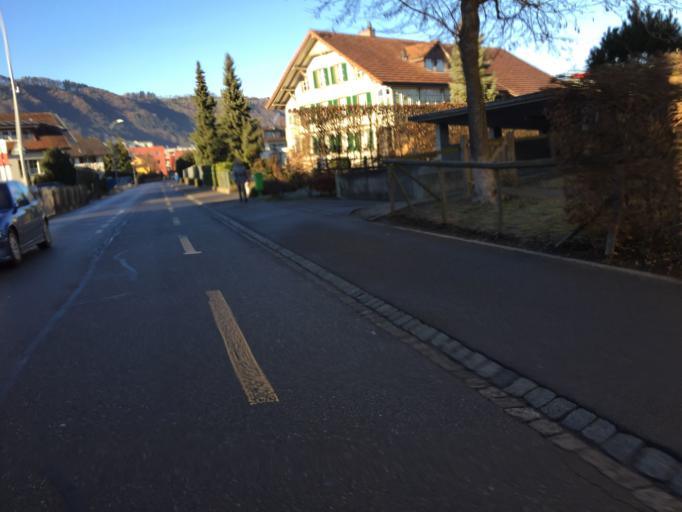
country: CH
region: Bern
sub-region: Bern-Mittelland District
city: Munsingen
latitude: 46.8738
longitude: 7.5549
